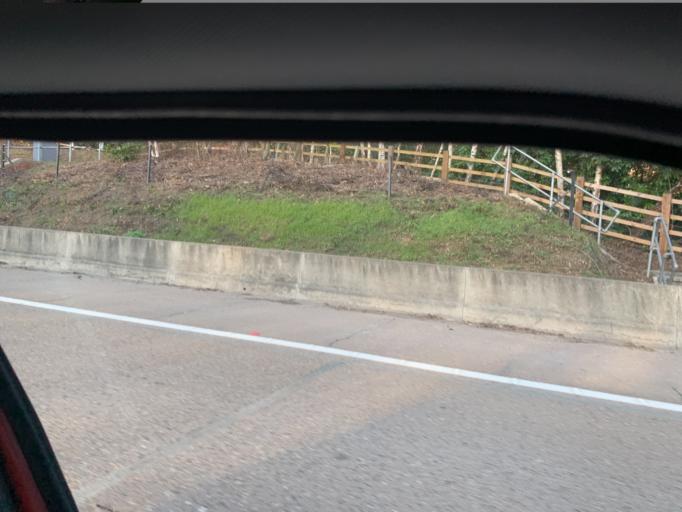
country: GB
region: England
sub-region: Surrey
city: Cobham
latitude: 51.3163
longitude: -0.4363
